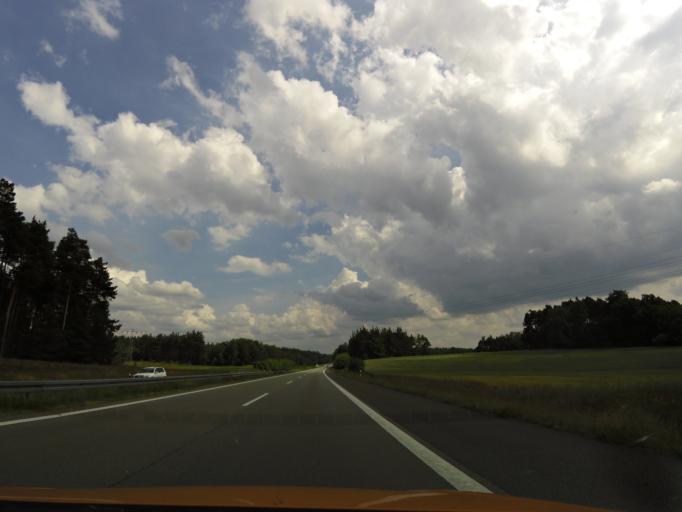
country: DE
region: Brandenburg
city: Heiligengrabe
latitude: 53.1621
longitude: 12.3850
